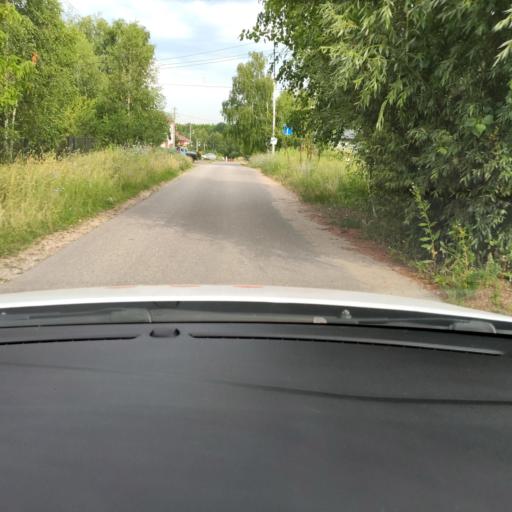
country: RU
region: Tatarstan
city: Stolbishchi
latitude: 55.7592
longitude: 49.2850
